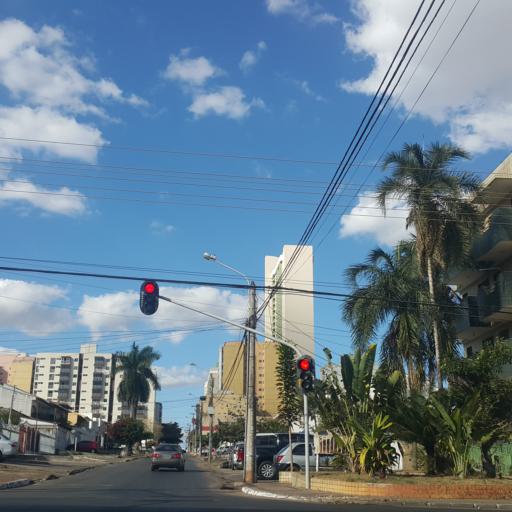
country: BR
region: Federal District
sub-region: Brasilia
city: Brasilia
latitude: -15.8276
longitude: -48.0629
